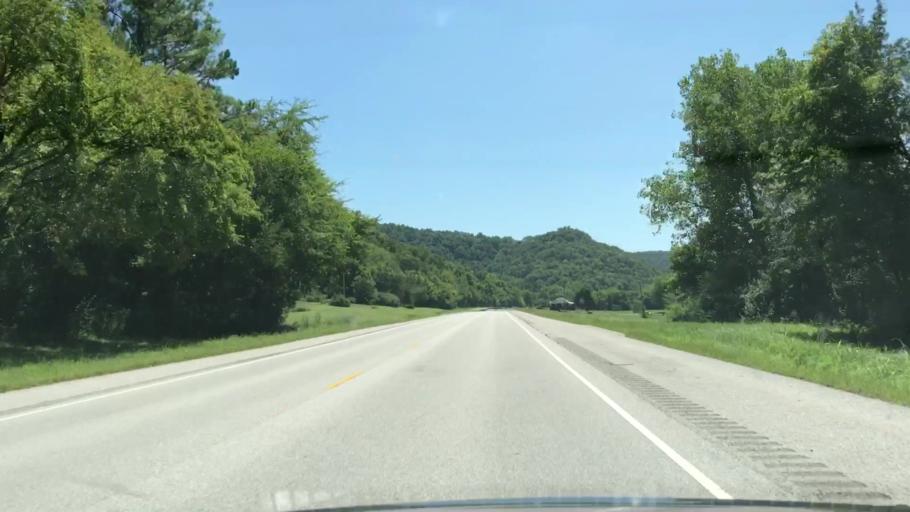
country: US
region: Tennessee
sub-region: Jackson County
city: Gainesboro
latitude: 36.4051
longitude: -85.6363
